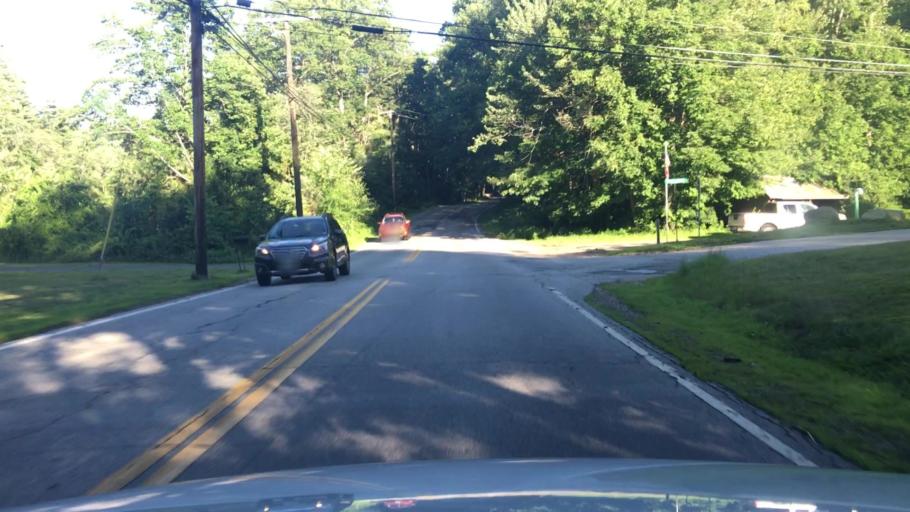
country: US
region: New Hampshire
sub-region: Rockingham County
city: Danville
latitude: 42.9050
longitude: -71.1515
